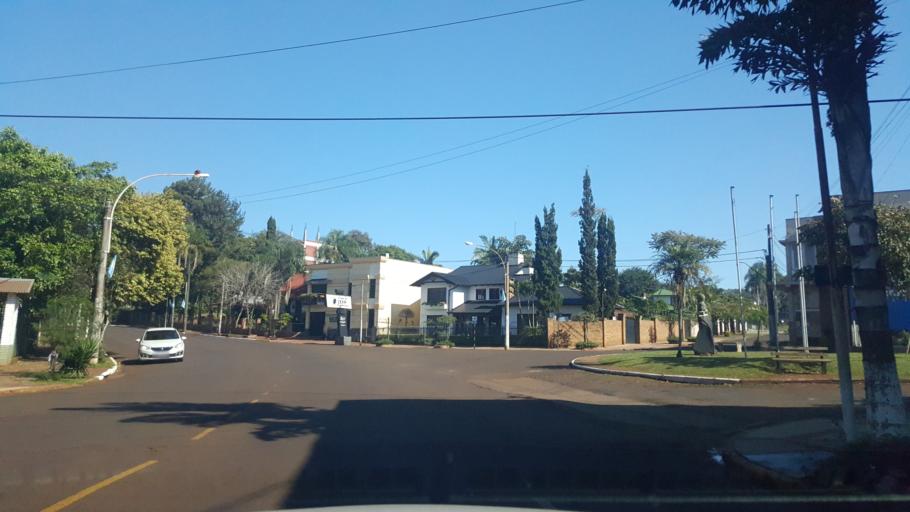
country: AR
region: Misiones
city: Puerto Rico
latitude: -26.8047
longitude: -55.0234
